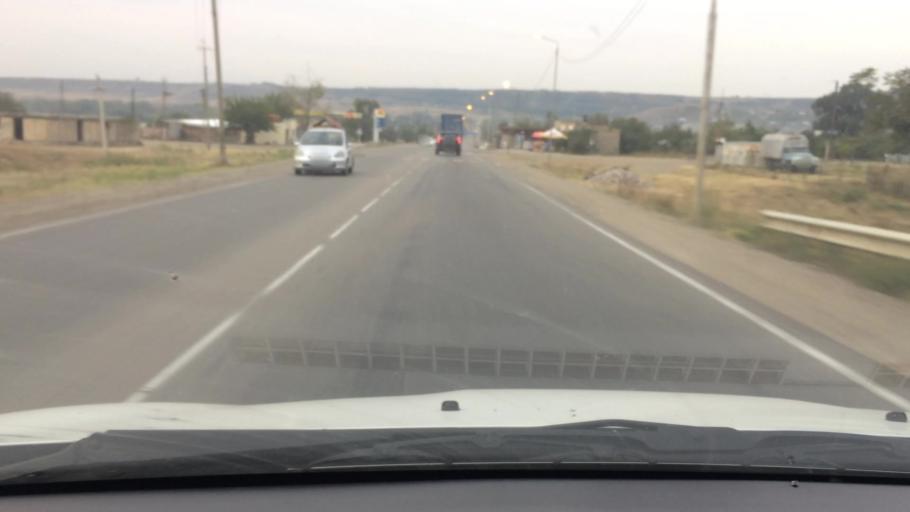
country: GE
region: T'bilisi
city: Tbilisi
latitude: 41.6195
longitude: 44.7947
